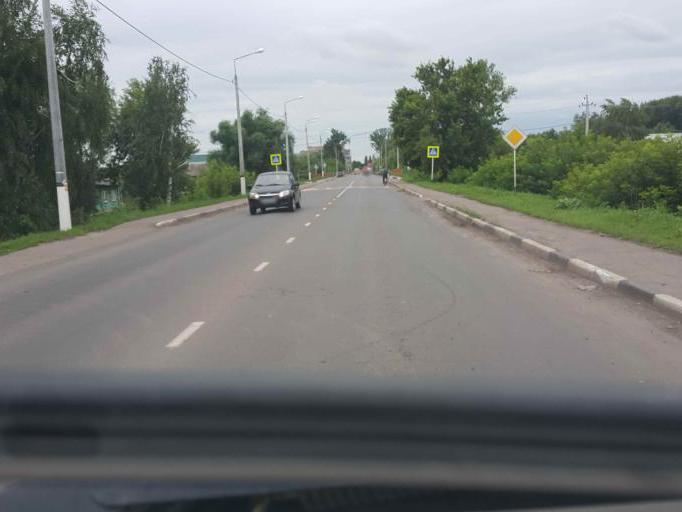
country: RU
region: Tambov
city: Zavoronezhskoye
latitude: 52.8829
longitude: 40.5384
